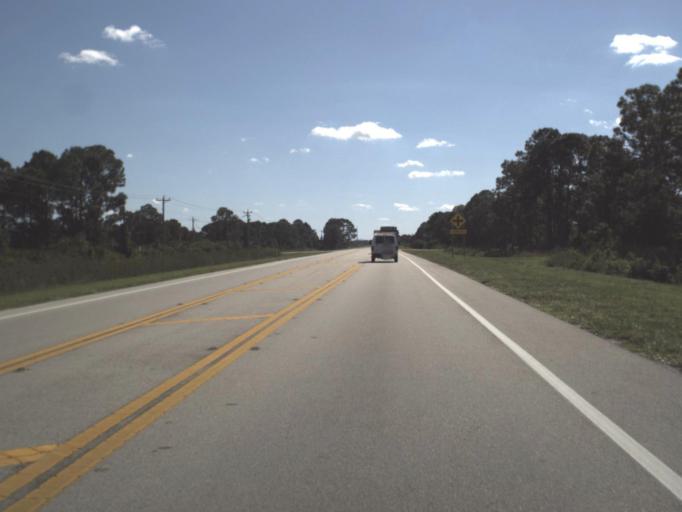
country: US
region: Florida
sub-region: Lee County
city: Lehigh Acres
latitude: 26.5213
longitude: -81.5752
